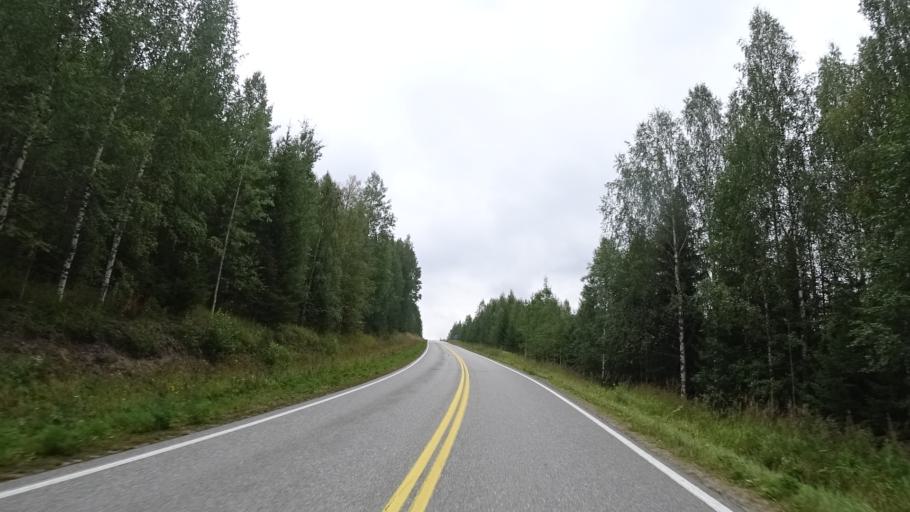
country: FI
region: North Karelia
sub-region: Pielisen Karjala
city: Lieksa
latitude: 63.2800
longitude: 30.5879
